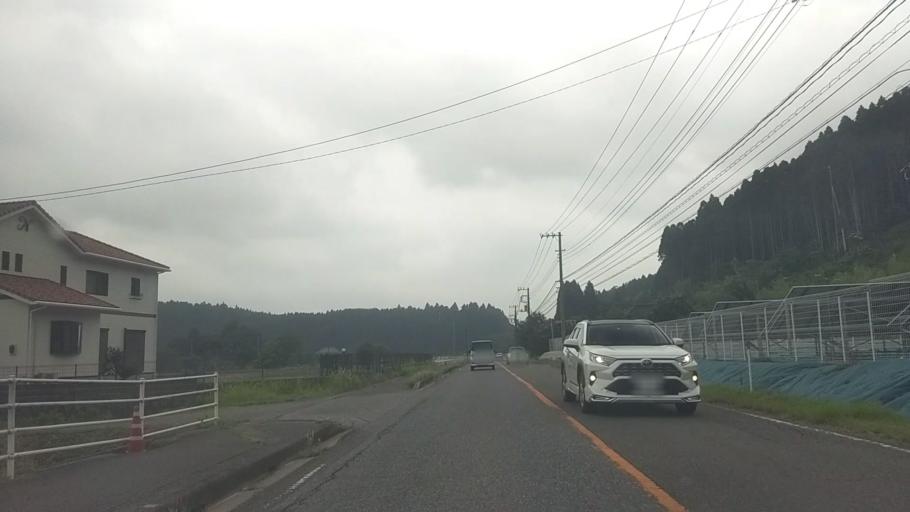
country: JP
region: Chiba
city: Ohara
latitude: 35.2727
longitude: 140.3310
